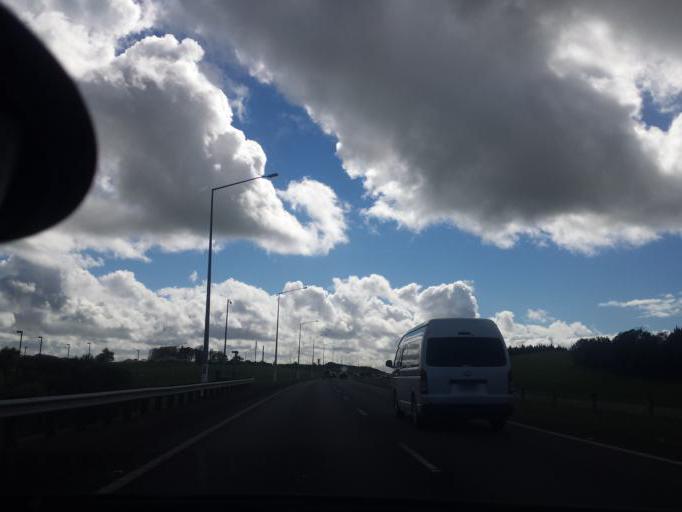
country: NZ
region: Auckland
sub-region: Auckland
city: Rothesay Bay
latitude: -36.6595
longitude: 174.6676
